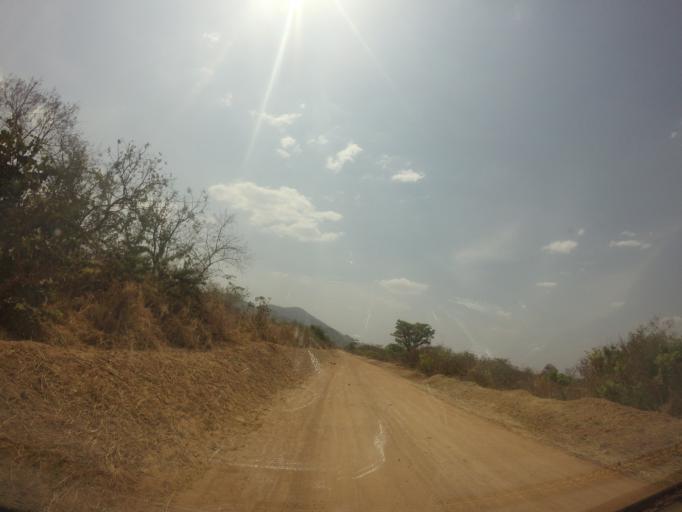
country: UG
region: Northern Region
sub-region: Arua District
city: Arua
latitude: 2.8971
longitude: 31.1243
